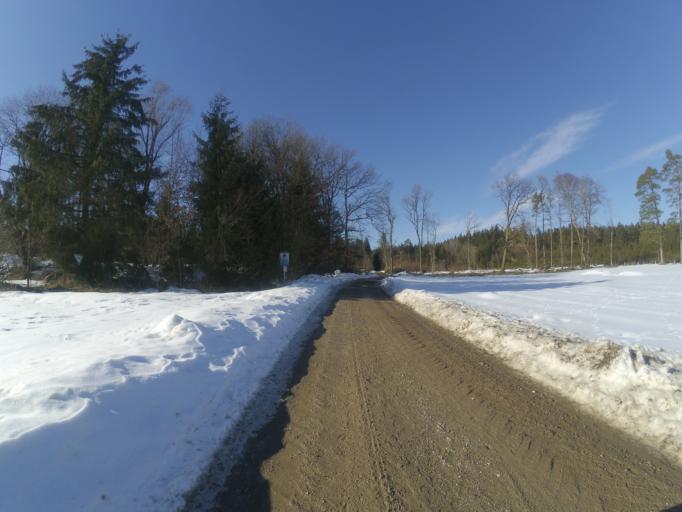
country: DE
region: Bavaria
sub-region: Upper Bavaria
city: Aying
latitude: 47.9816
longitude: 11.7605
